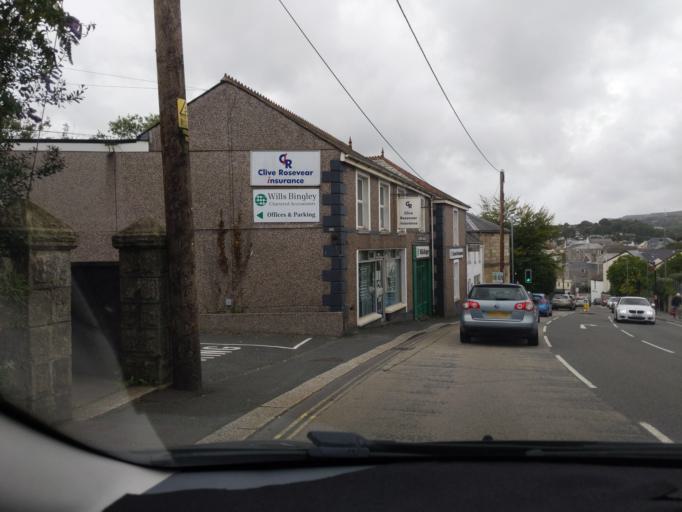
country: GB
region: England
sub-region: Cornwall
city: St Austell
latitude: 50.3376
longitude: -4.7891
